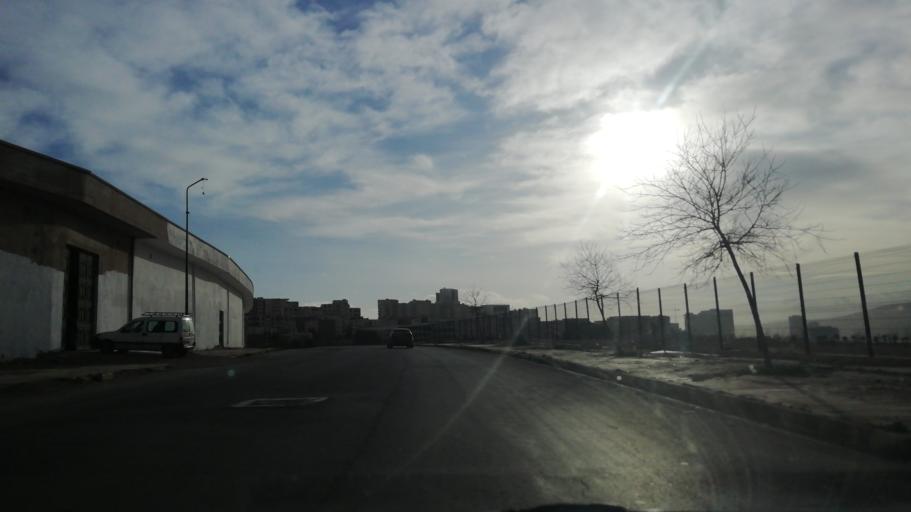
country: DZ
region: Oran
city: Bir el Djir
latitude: 35.7226
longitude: -0.5952
